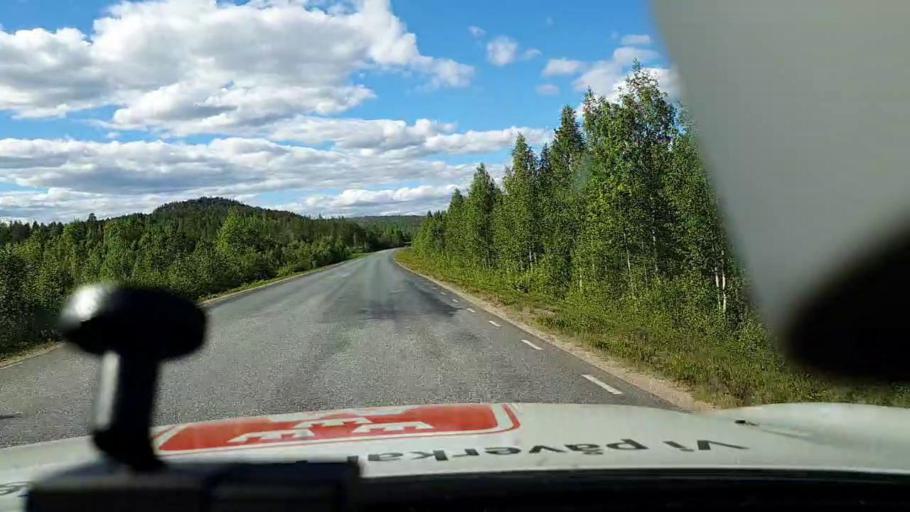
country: FI
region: Lapland
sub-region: Torniolaakso
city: Ylitornio
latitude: 66.3015
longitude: 23.6313
